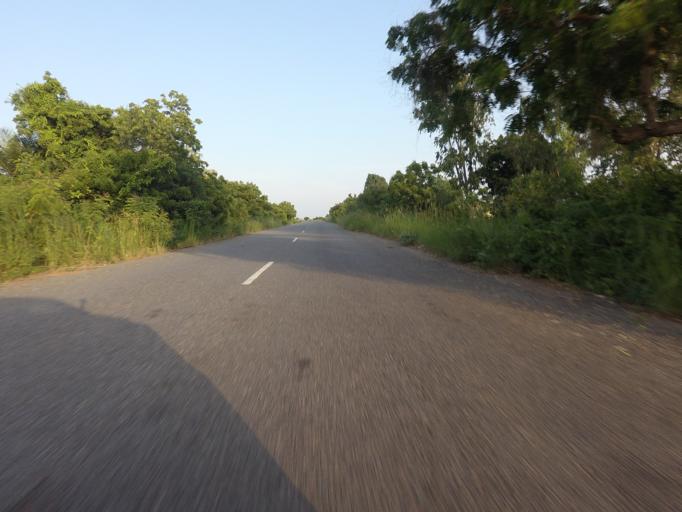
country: GH
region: Volta
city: Anloga
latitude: 5.8576
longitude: 0.7661
